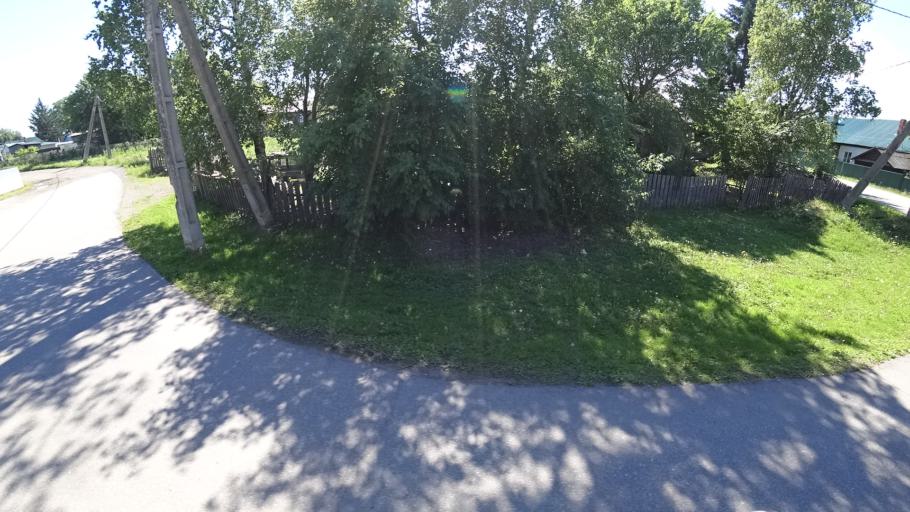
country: RU
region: Khabarovsk Krai
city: Khor
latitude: 47.8888
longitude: 135.0351
